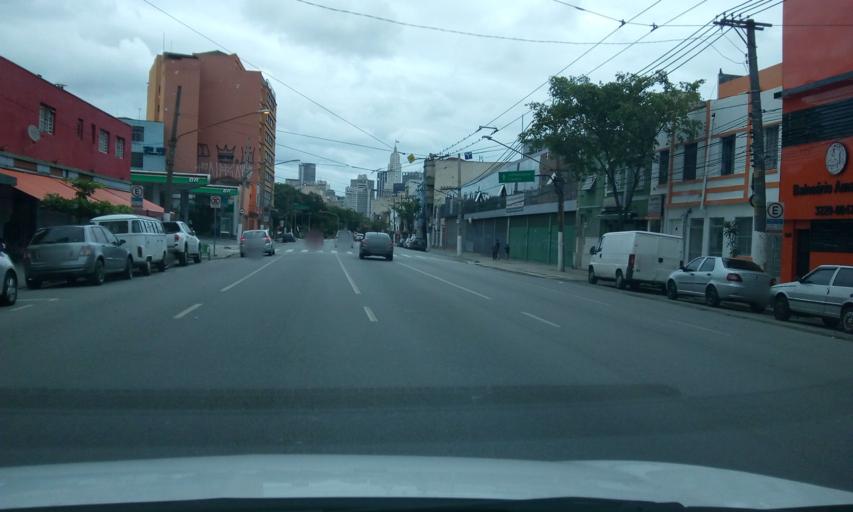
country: BR
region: Sao Paulo
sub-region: Sao Paulo
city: Sao Paulo
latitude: -23.5436
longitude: -46.6198
